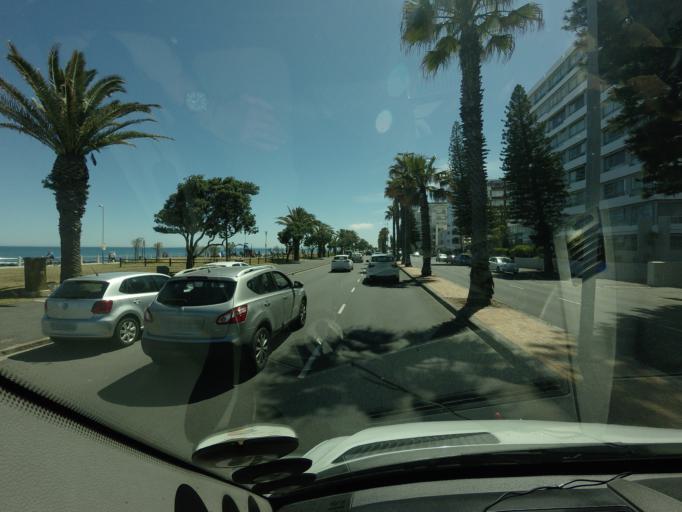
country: ZA
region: Western Cape
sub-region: City of Cape Town
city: Cape Town
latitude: -33.9150
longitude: 18.3871
